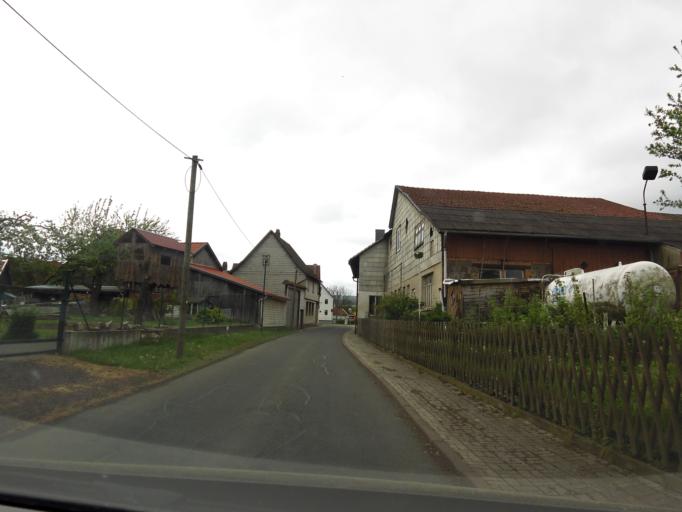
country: DE
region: Thuringia
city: Ernstroda
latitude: 50.8809
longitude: 10.6139
